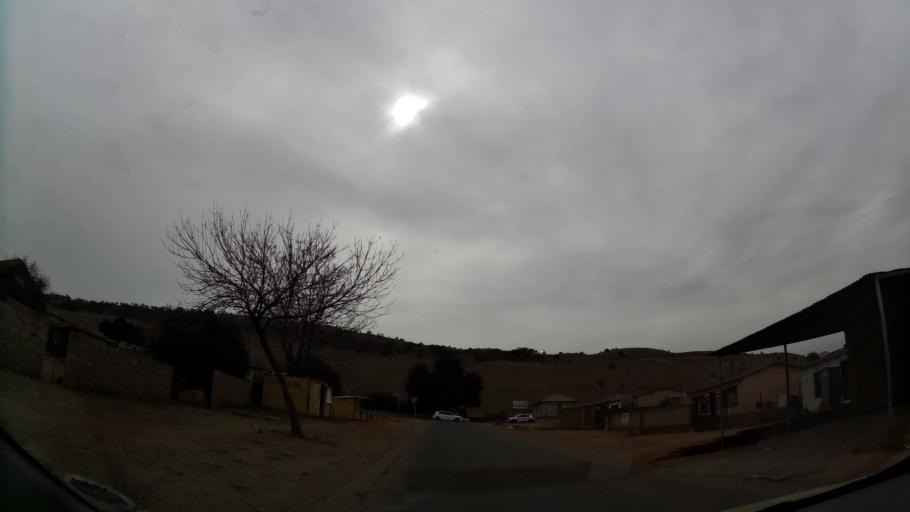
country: ZA
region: Gauteng
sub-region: City of Tshwane Metropolitan Municipality
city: Pretoria
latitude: -25.7019
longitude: 28.3361
